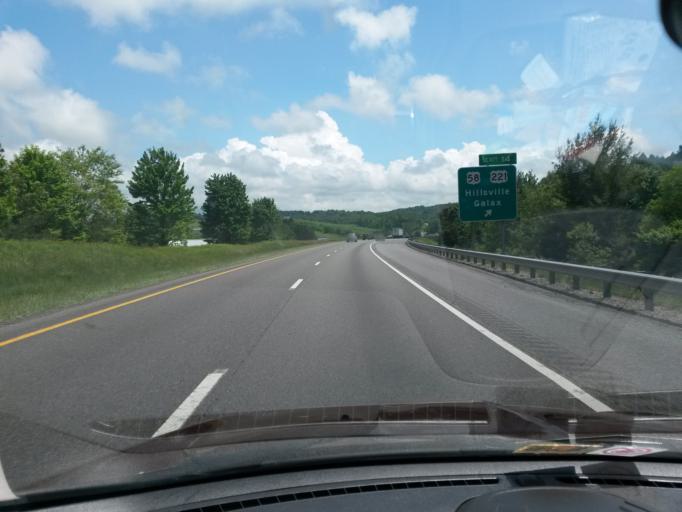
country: US
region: Virginia
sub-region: Carroll County
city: Hillsville
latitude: 36.7505
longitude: -80.7749
